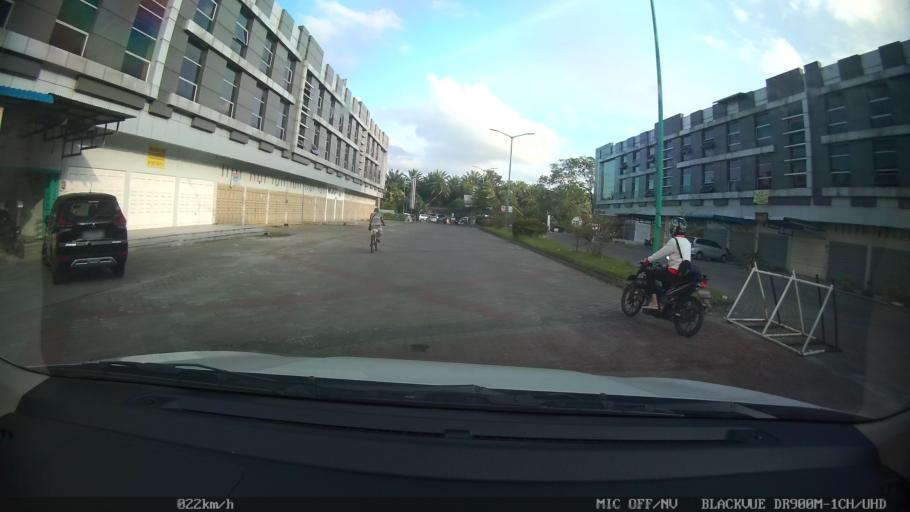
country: ID
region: North Sumatra
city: Medan
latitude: 3.6229
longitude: 98.6585
